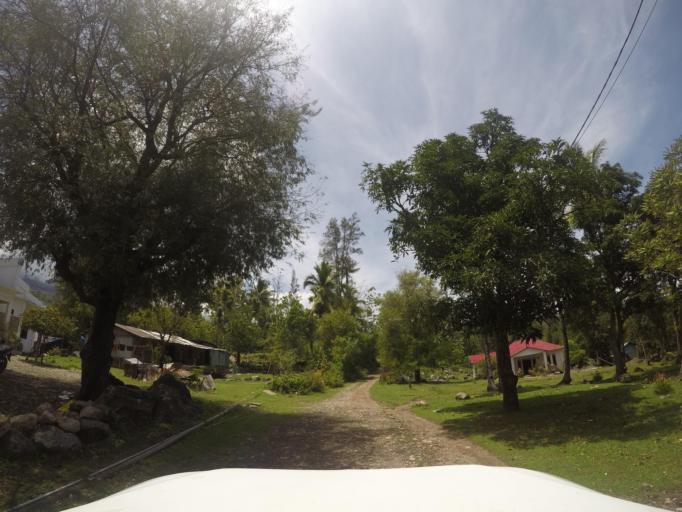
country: TL
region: Bobonaro
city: Maliana
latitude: -8.9985
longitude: 125.2251
